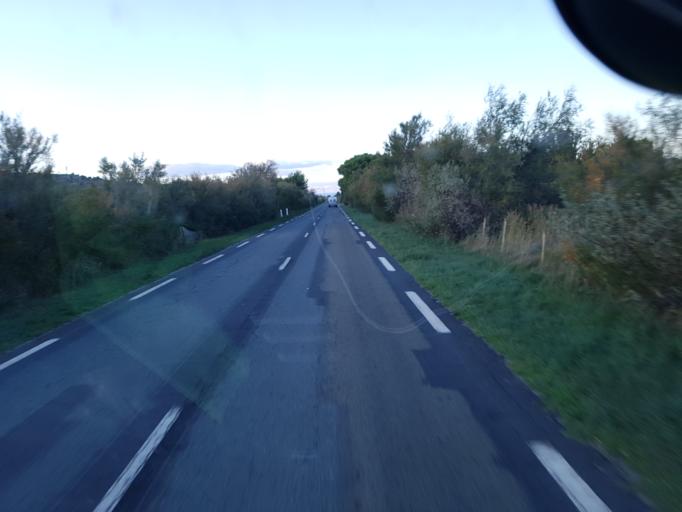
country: FR
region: Languedoc-Roussillon
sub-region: Departement de l'Aude
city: Port-la-Nouvelle
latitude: 43.0049
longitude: 3.0394
